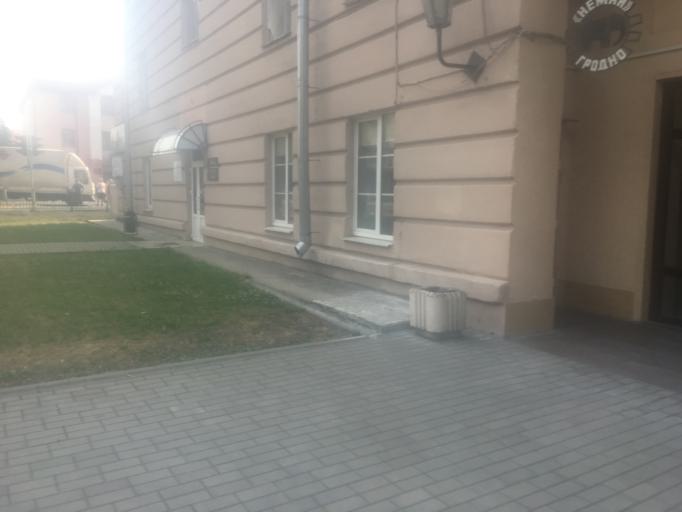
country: BY
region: Grodnenskaya
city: Hrodna
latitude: 53.6717
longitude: 23.8073
